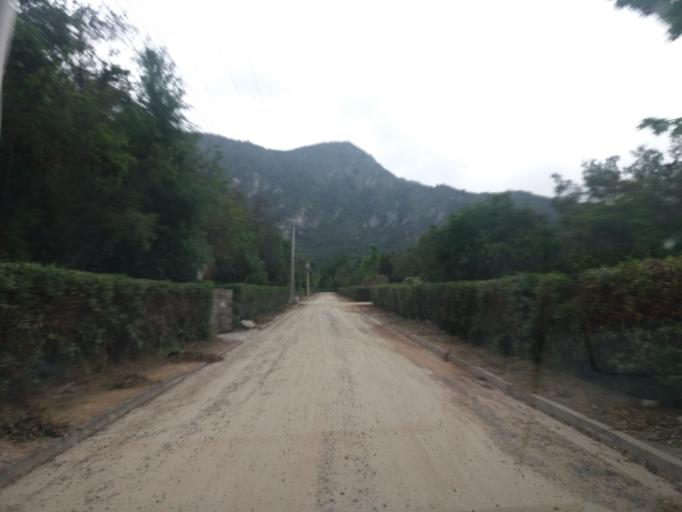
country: CL
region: Valparaiso
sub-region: Provincia de Marga Marga
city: Limache
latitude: -33.0240
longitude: -71.1374
